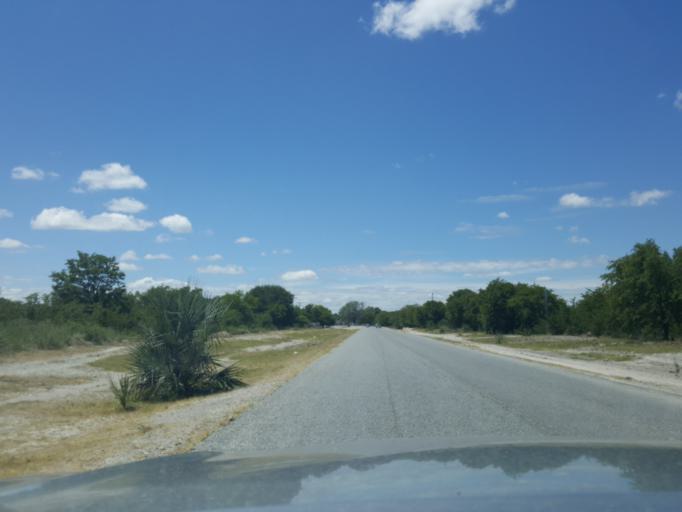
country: BW
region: Central
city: Nata
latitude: -20.2125
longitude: 26.1751
